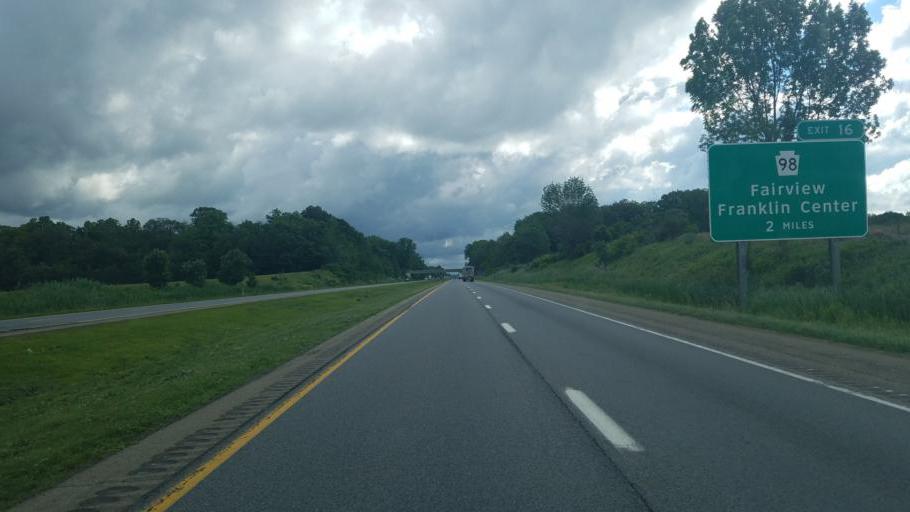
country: US
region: Pennsylvania
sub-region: Erie County
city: Girard
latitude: 41.9895
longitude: -80.2752
